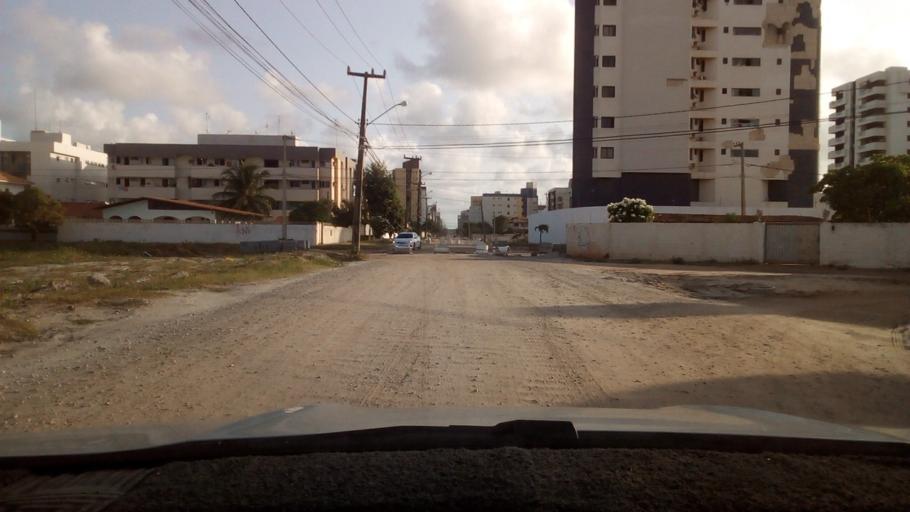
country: BR
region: Paraiba
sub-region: Cabedelo
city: Cabedelo
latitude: -7.0359
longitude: -34.8411
